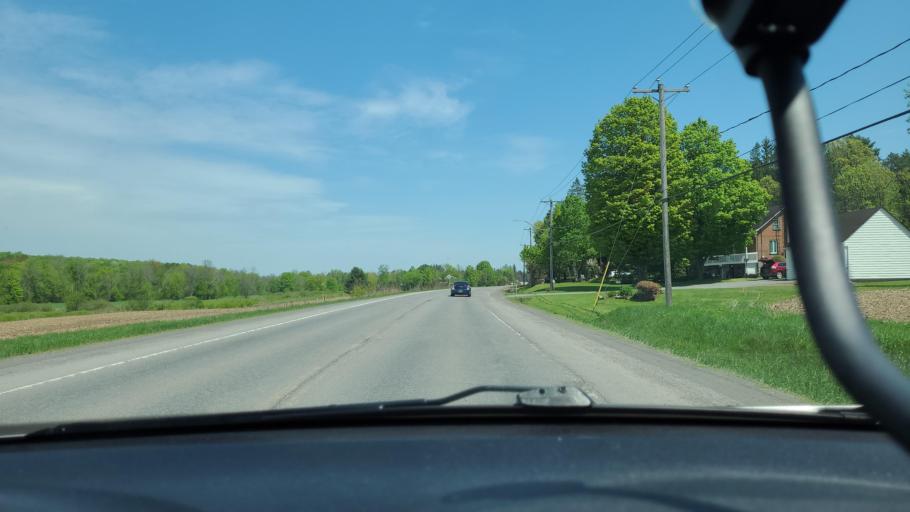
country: CA
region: Quebec
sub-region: Laurentides
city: Lachute
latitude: 45.6675
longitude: -74.2788
